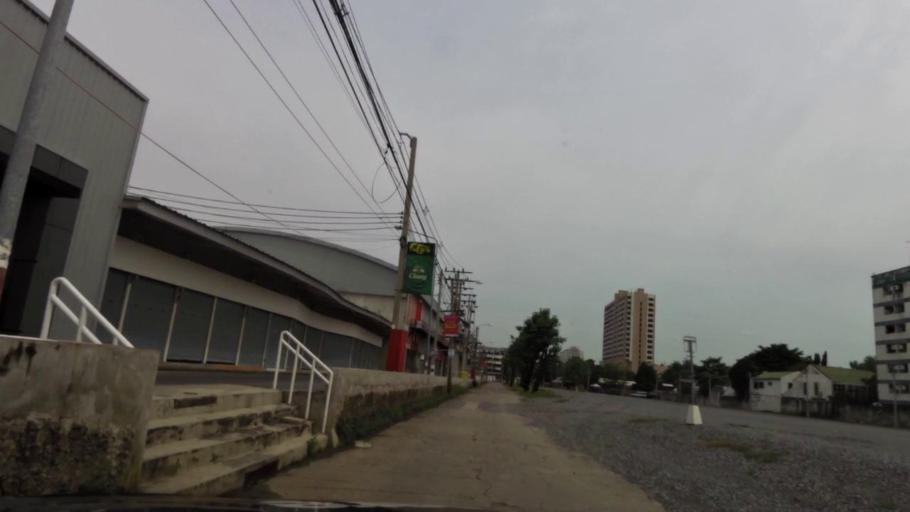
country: TH
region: Bangkok
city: Bang Kapi
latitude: 13.7666
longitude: 100.6390
